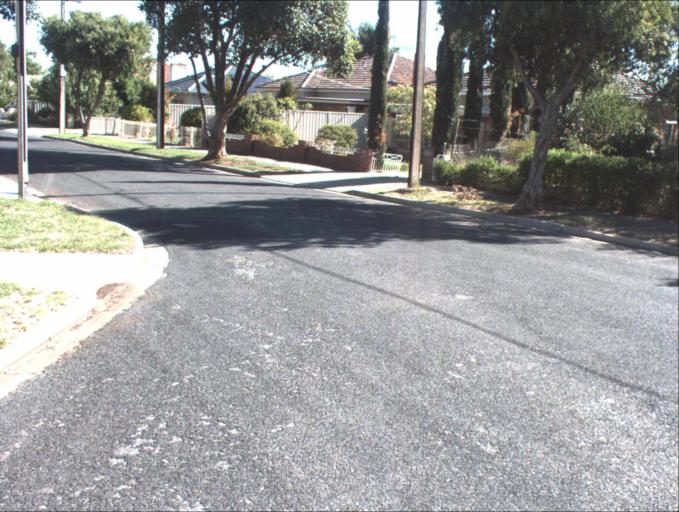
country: AU
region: South Australia
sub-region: Prospect
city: Prospect
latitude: -34.8743
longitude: 138.6128
